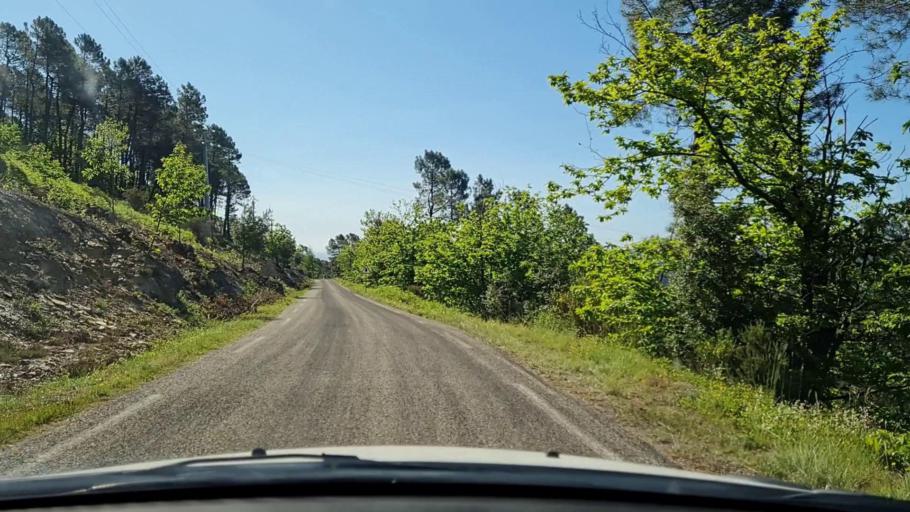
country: FR
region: Languedoc-Roussillon
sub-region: Departement du Gard
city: Branoux-les-Taillades
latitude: 44.1872
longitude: 3.9826
